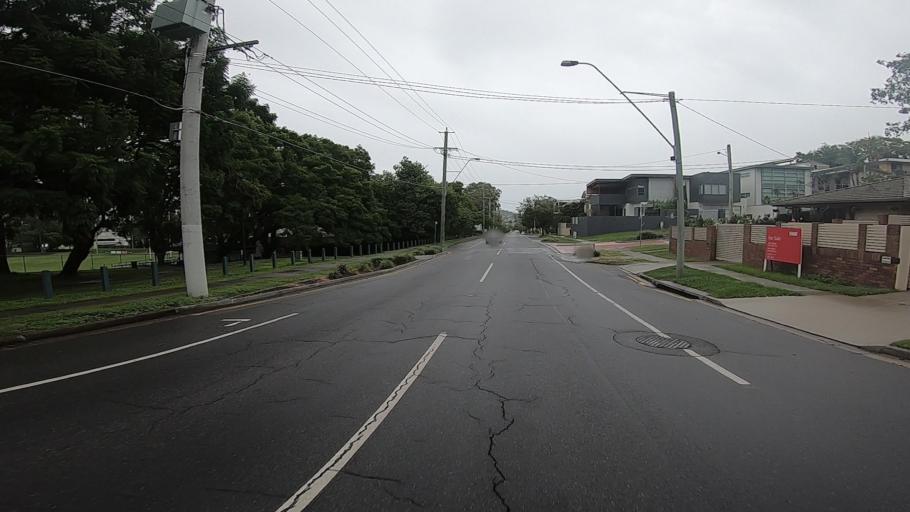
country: AU
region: Queensland
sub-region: Brisbane
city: Ascot
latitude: -27.4326
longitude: 153.0484
